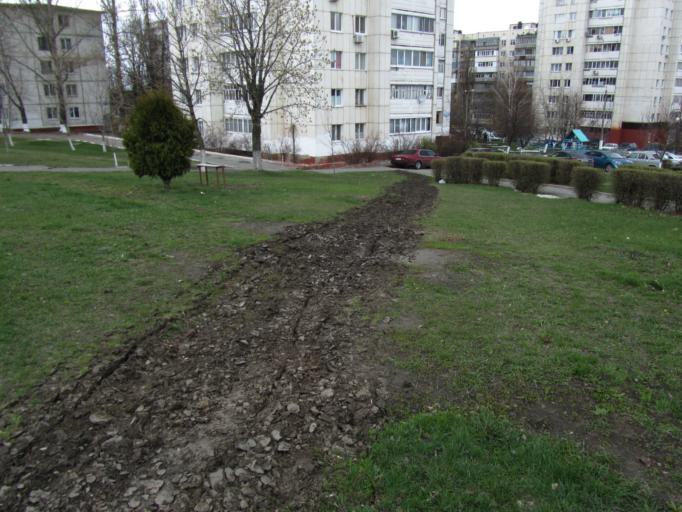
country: RU
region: Belgorod
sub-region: Belgorodskiy Rayon
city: Belgorod
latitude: 50.5790
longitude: 36.5823
